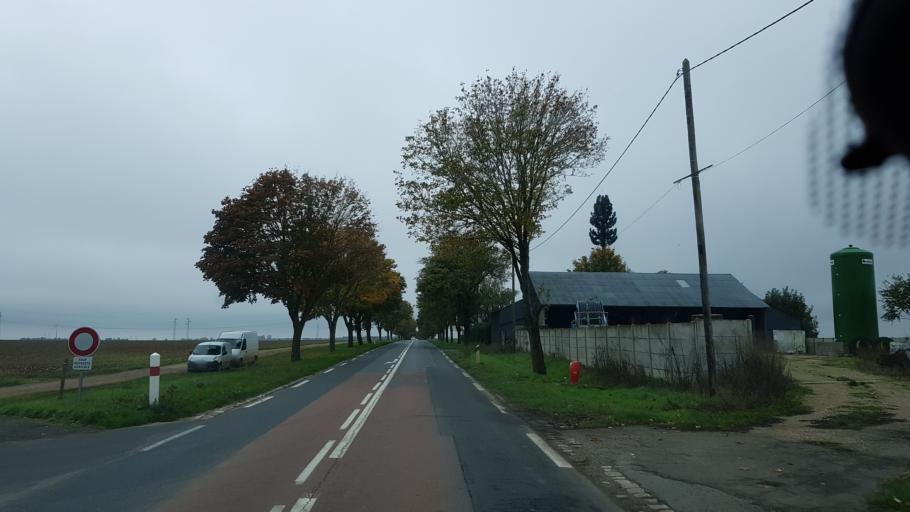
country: FR
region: Ile-de-France
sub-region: Departement de l'Essonne
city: Pussay
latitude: 48.3436
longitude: 1.9885
